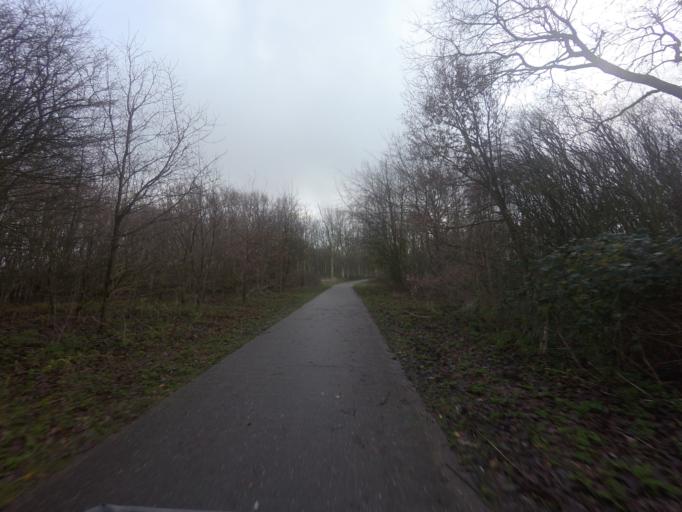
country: NL
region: North Holland
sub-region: Gemeente Texel
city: Den Burg
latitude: 53.1636
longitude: 4.8516
